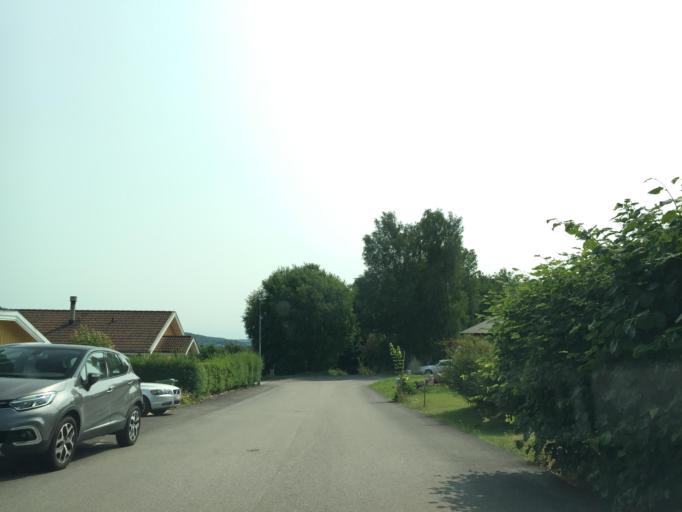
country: SE
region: Vaestra Goetaland
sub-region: Lilla Edets Kommun
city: Lilla Edet
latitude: 58.1791
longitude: 12.1085
